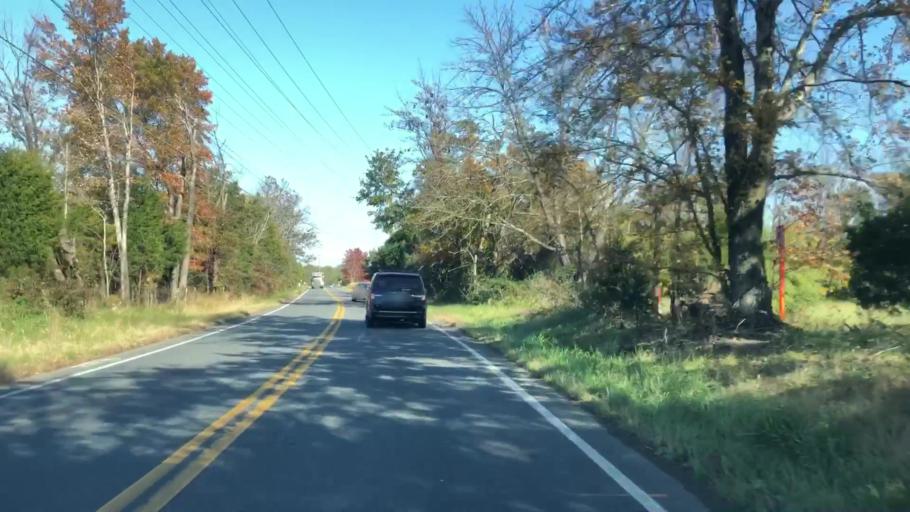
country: US
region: Virginia
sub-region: Prince William County
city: Gainesville
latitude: 38.7514
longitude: -77.6452
